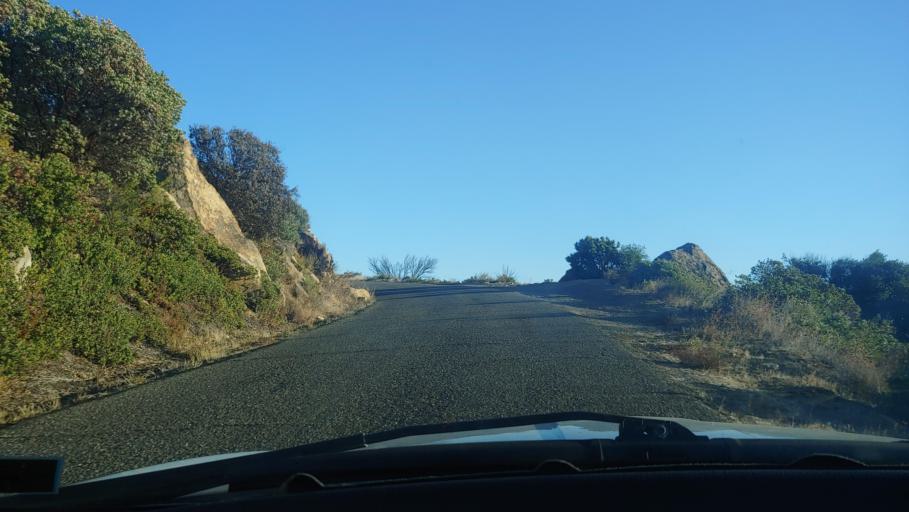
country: US
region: California
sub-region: Santa Barbara County
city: Mission Canyon
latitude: 34.5094
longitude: -119.7725
